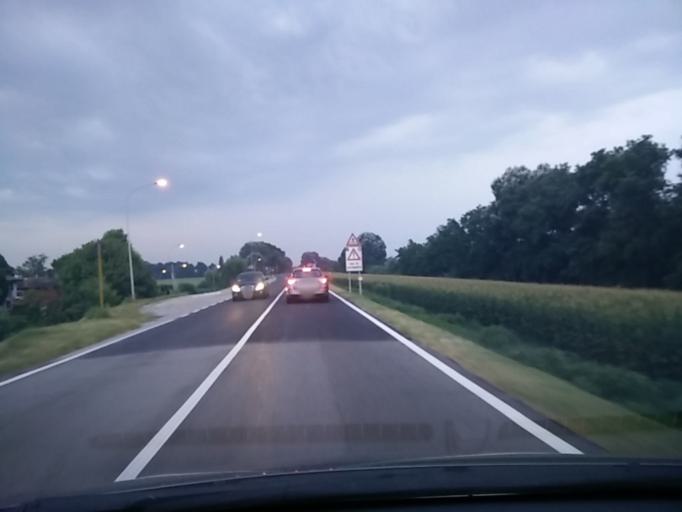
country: IT
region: Veneto
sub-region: Provincia di Venezia
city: Passarella
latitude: 45.5951
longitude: 12.6225
